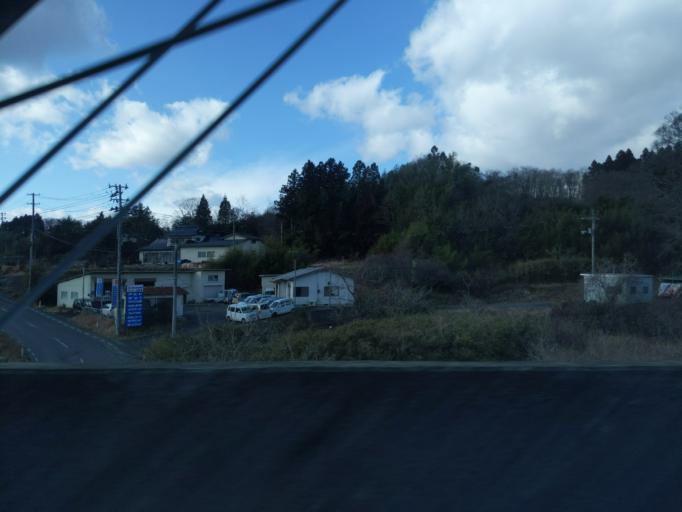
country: JP
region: Miyagi
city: Kogota
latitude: 38.7062
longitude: 141.0474
